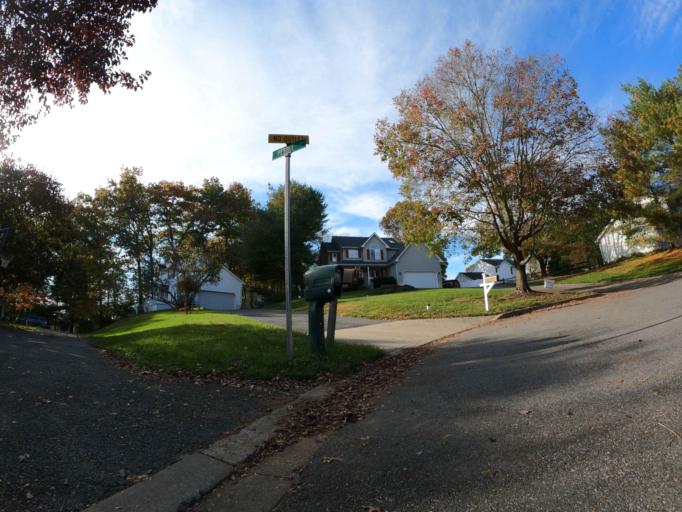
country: US
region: Maryland
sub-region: Carroll County
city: Sykesville
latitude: 39.3651
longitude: -76.9729
